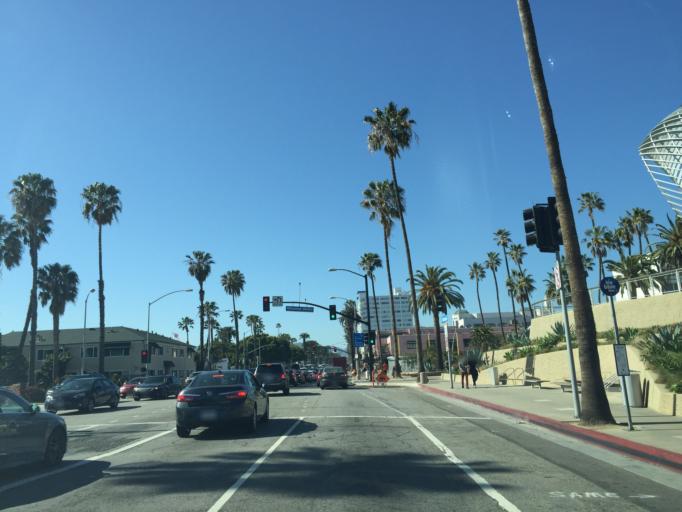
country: US
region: California
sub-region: Los Angeles County
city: Santa Monica
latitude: 34.0106
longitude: -118.4938
